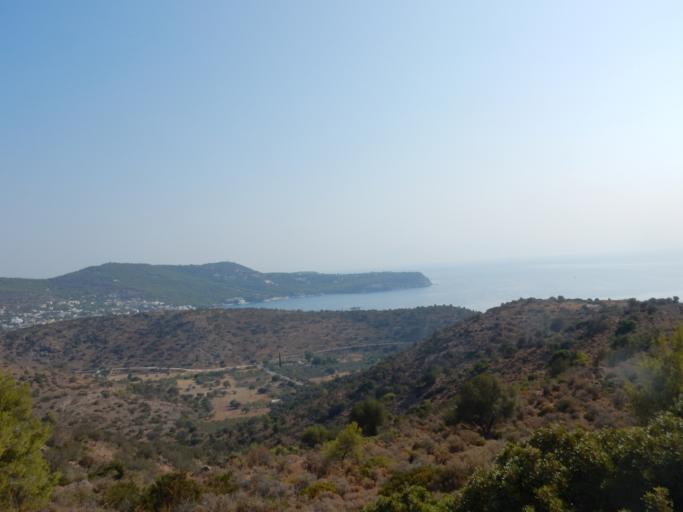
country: GR
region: Attica
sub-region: Nomos Piraios
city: Vathi
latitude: 37.7279
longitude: 23.5305
